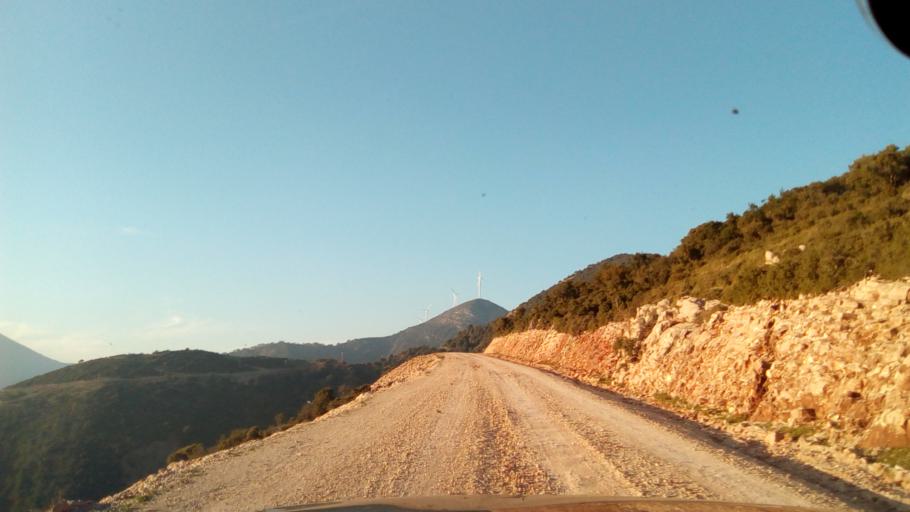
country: GR
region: West Greece
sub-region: Nomos Aitolias kai Akarnanias
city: Nafpaktos
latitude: 38.4351
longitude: 21.8491
